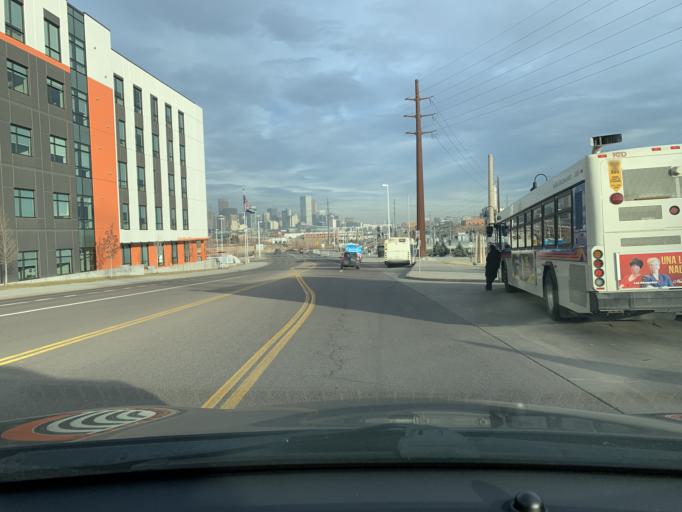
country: US
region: Colorado
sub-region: Denver County
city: Denver
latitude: 39.7380
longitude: -105.0240
